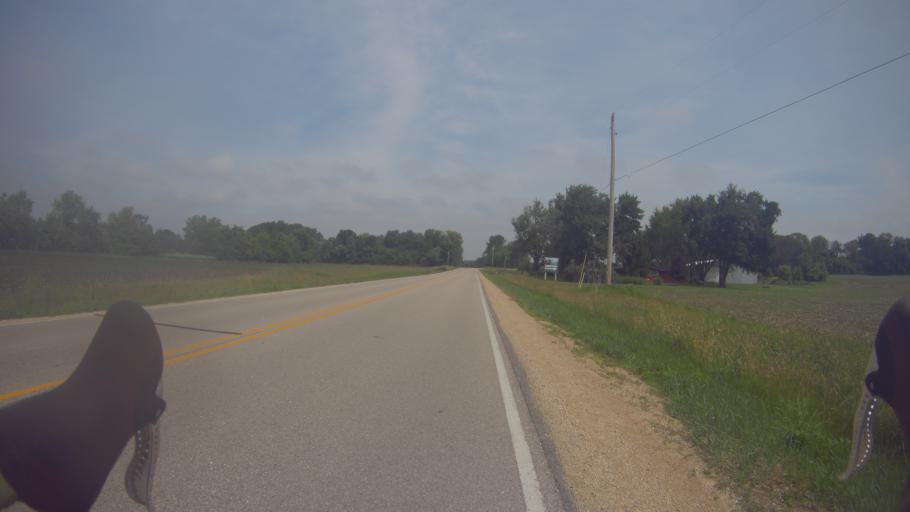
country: US
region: Wisconsin
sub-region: Rock County
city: Edgerton
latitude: 42.8639
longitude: -89.0314
